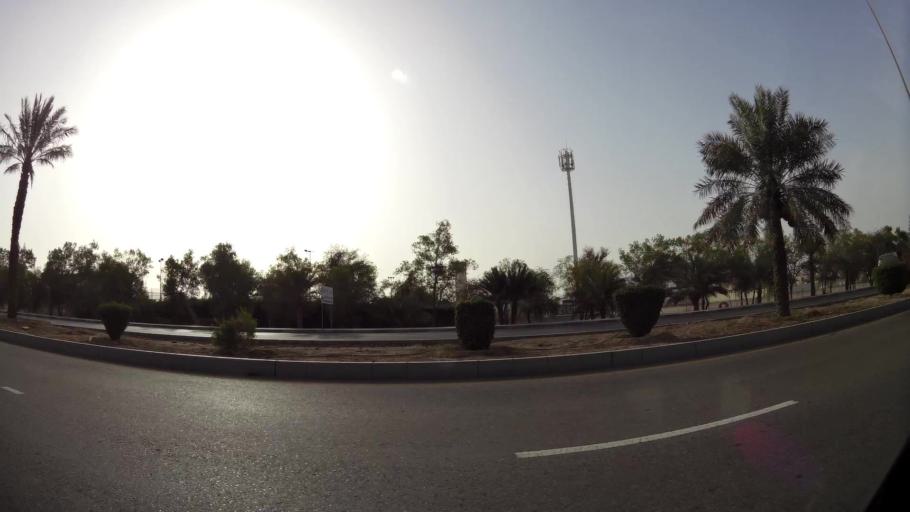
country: AE
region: Abu Dhabi
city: Al Ain
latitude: 24.1274
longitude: 55.7072
